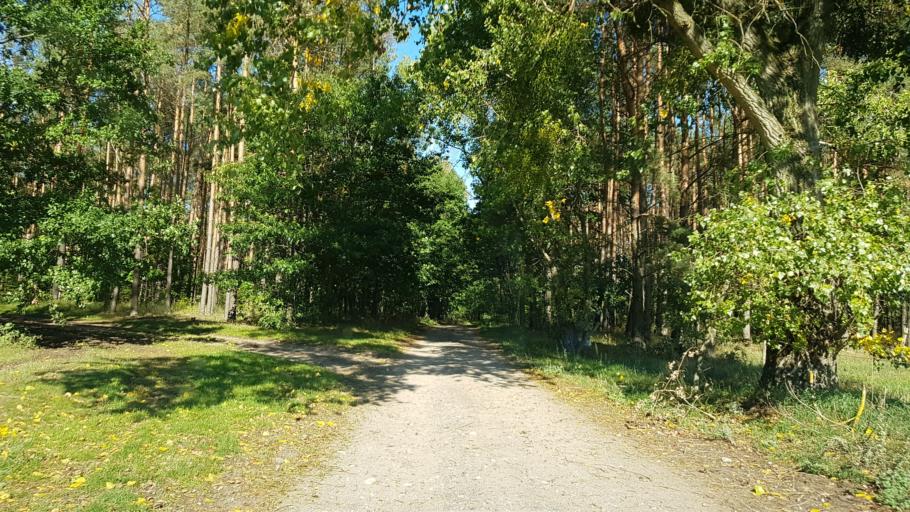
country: PL
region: Lubusz
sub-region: Powiat gorzowski
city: Lubiszyn
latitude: 52.8409
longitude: 14.9308
